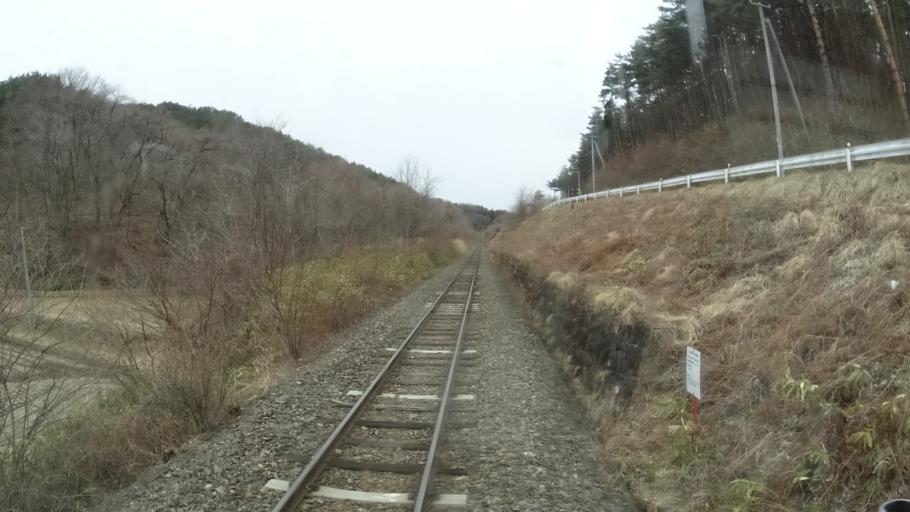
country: JP
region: Iwate
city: Tono
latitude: 39.3195
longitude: 141.3679
